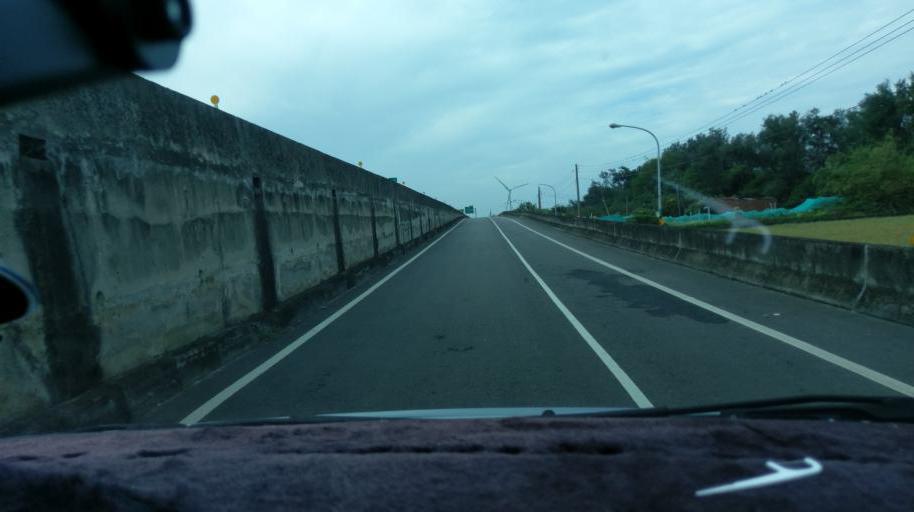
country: TW
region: Taiwan
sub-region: Hsinchu
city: Hsinchu
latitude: 24.7317
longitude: 120.8784
